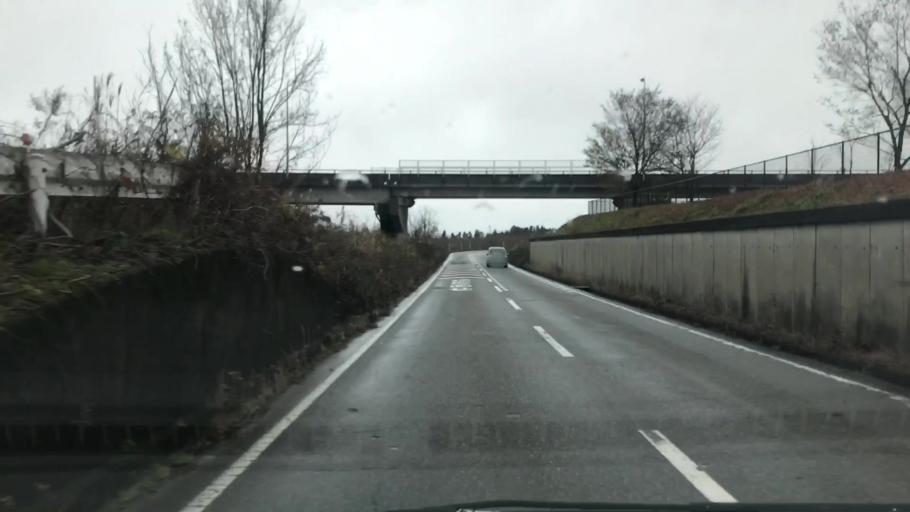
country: JP
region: Toyama
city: Kamiichi
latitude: 36.6261
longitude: 137.3008
